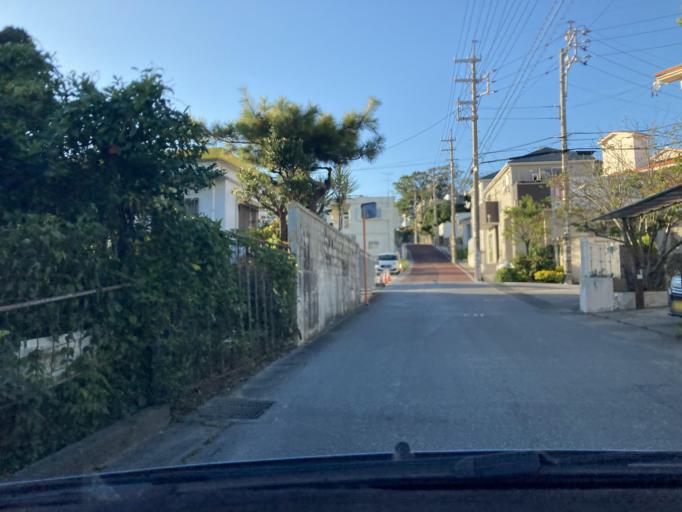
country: JP
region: Okinawa
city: Naha-shi
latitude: 26.2144
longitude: 127.7270
